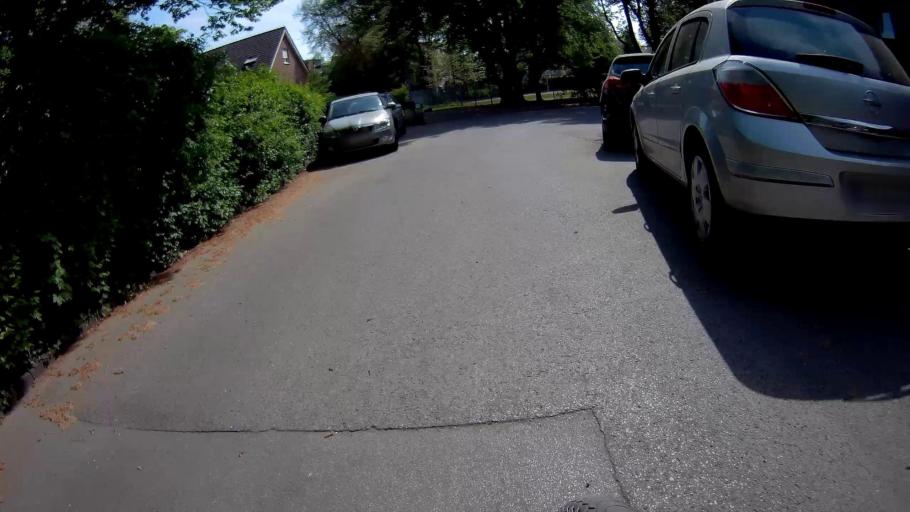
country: DE
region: North Rhine-Westphalia
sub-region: Regierungsbezirk Munster
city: Gelsenkirchen
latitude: 51.5605
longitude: 7.0859
